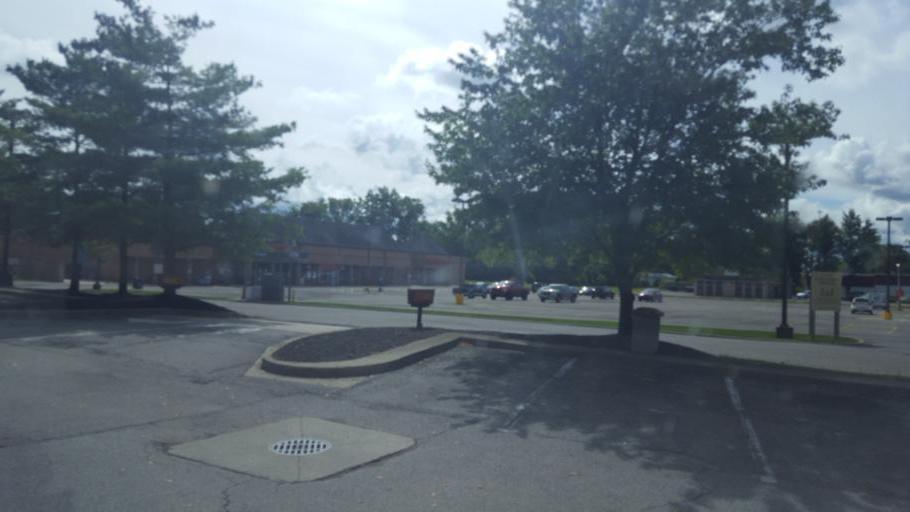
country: US
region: Ohio
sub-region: Lorain County
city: Oberlin
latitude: 41.2843
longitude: -82.2174
